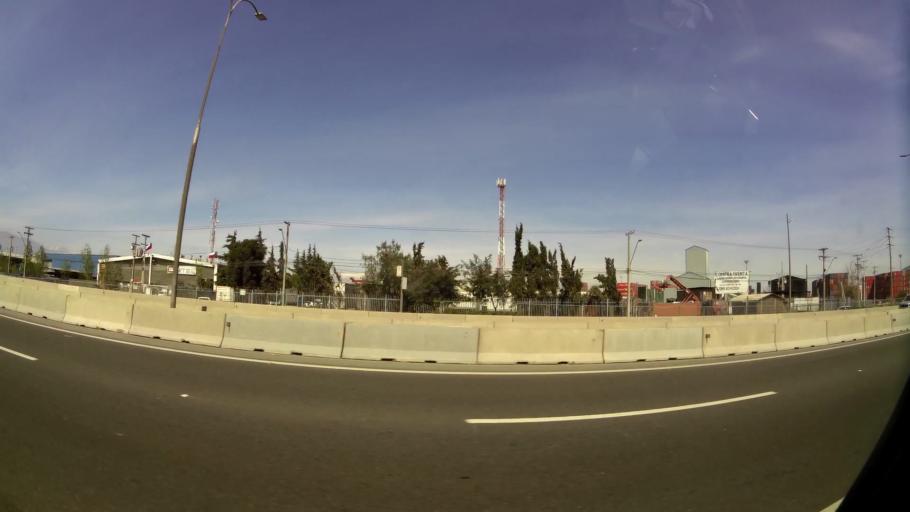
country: CL
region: Santiago Metropolitan
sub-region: Provincia de Maipo
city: San Bernardo
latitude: -33.5474
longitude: -70.6963
